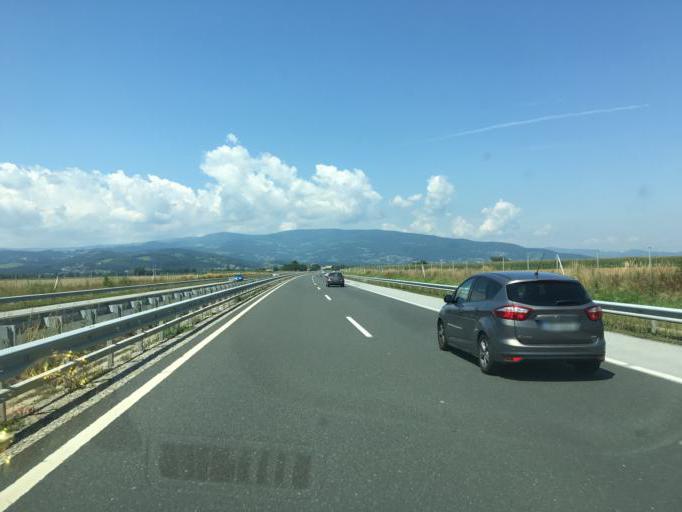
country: SI
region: Race-Fram
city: Race
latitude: 46.4611
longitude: 15.7033
